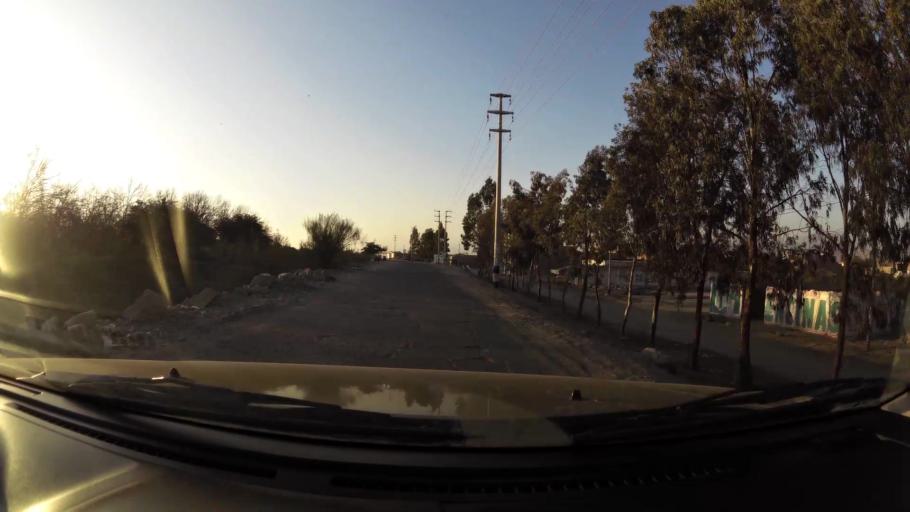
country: PE
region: Ica
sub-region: Provincia de Ica
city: Ica
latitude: -14.0812
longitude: -75.7182
